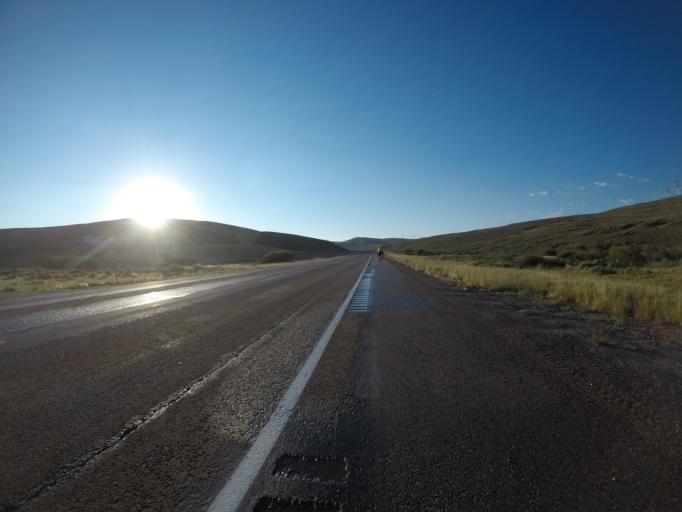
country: US
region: Wyoming
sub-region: Lincoln County
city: Kemmerer
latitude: 41.8706
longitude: -110.5115
